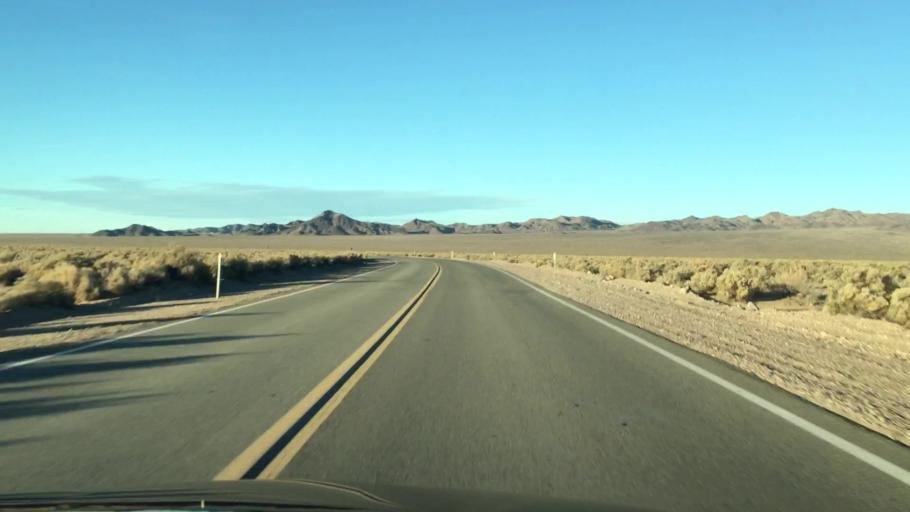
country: US
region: California
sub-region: San Bernardino County
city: Fort Irwin
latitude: 35.3274
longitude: -116.0809
